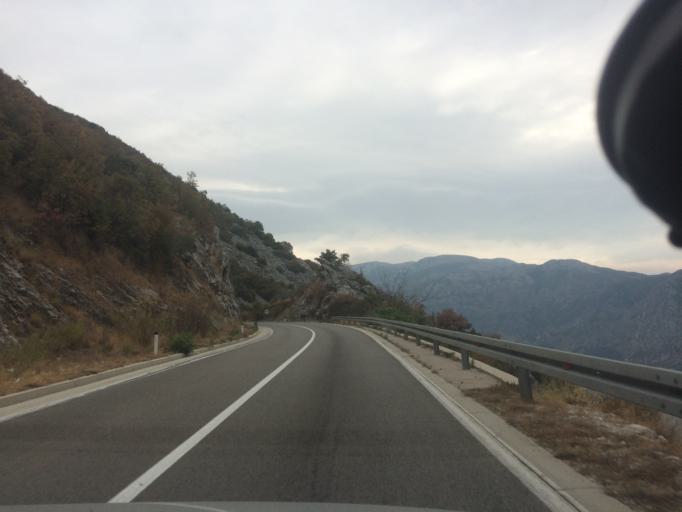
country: ME
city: Lipci
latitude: 42.5004
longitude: 18.6544
